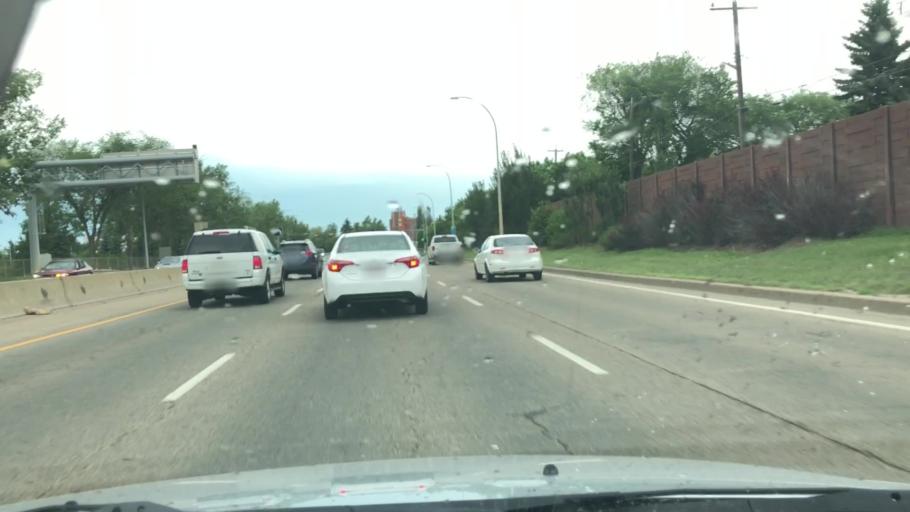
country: CA
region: Alberta
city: Edmonton
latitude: 53.5663
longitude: -113.4498
